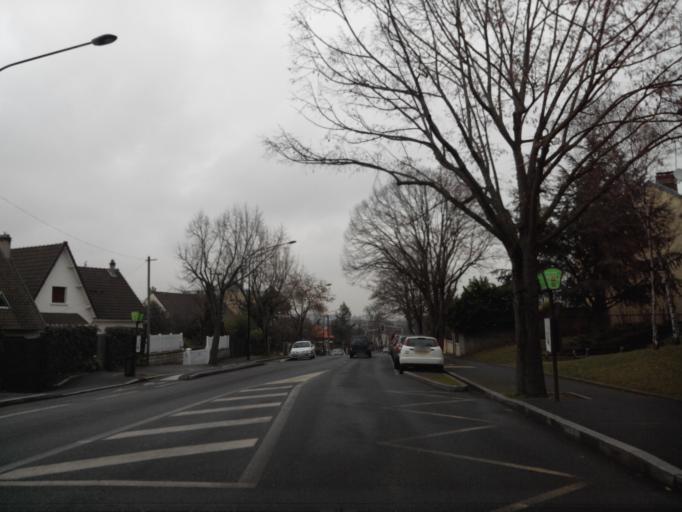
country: FR
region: Ile-de-France
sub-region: Departement du Val-de-Marne
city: L'Hay-les-Roses
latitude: 48.7874
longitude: 2.3373
